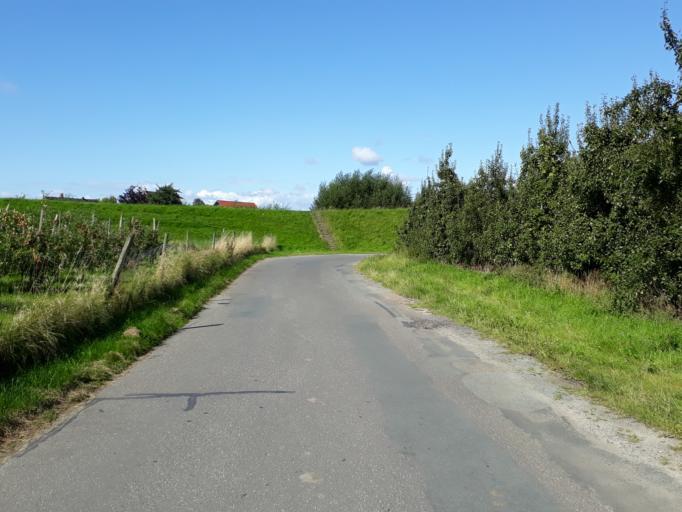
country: DE
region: Lower Saxony
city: Grunendeich
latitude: 53.5657
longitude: 9.6220
